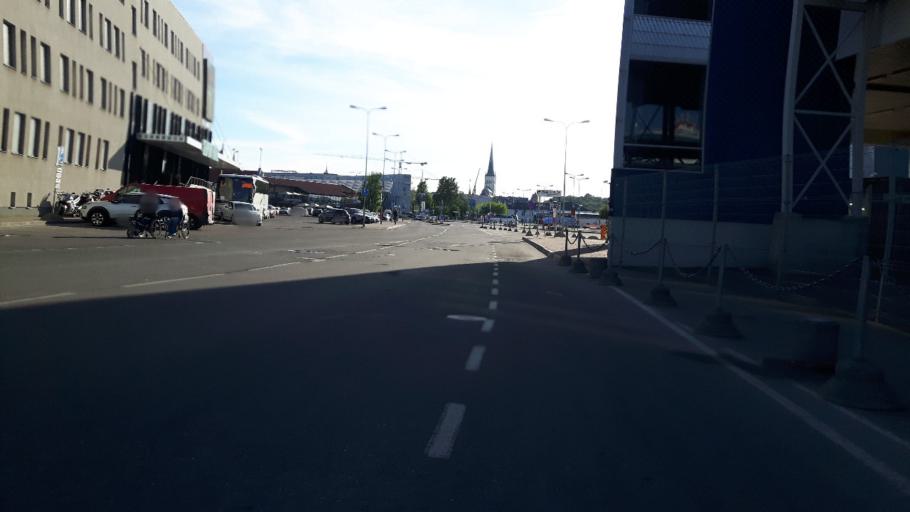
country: EE
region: Harju
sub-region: Tallinna linn
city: Tallinn
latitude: 59.4431
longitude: 24.7682
